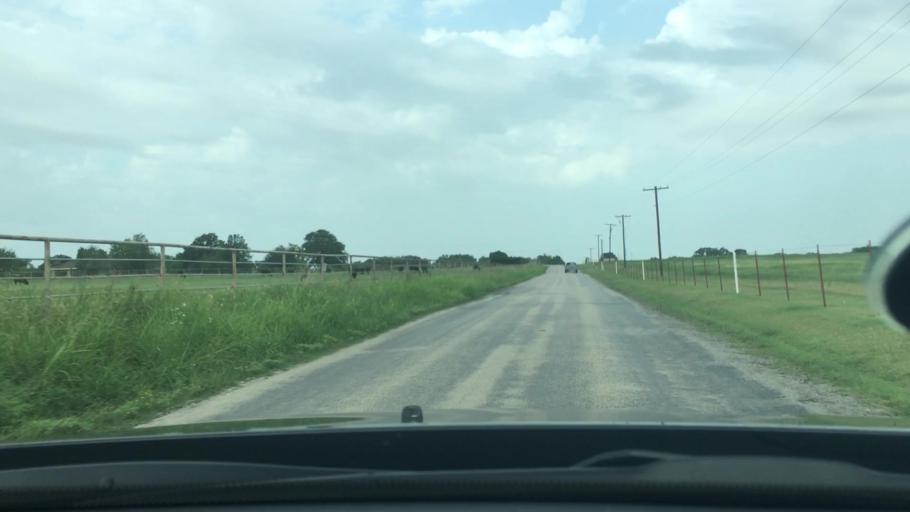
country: US
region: Oklahoma
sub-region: Carter County
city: Lone Grove
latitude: 34.2020
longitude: -97.2568
